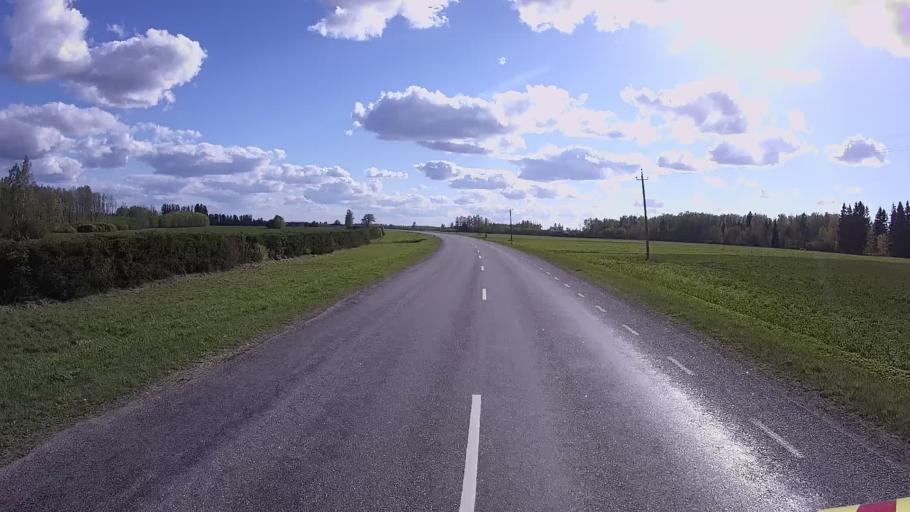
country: EE
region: Jogevamaa
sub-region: Poltsamaa linn
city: Poltsamaa
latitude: 58.6969
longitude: 26.1386
